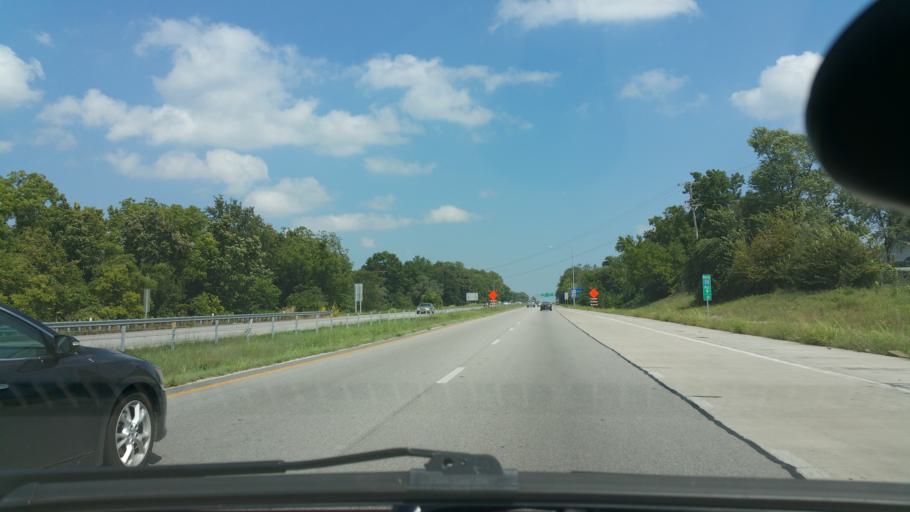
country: US
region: Missouri
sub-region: Clay County
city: Gladstone
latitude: 39.1763
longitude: -94.5324
